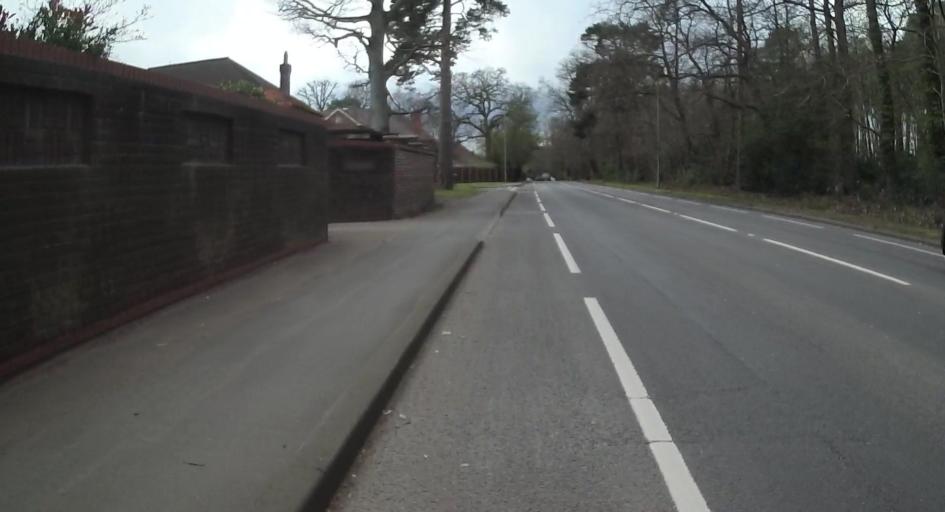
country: GB
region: England
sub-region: Surrey
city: West Byfleet
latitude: 51.3387
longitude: -0.5275
